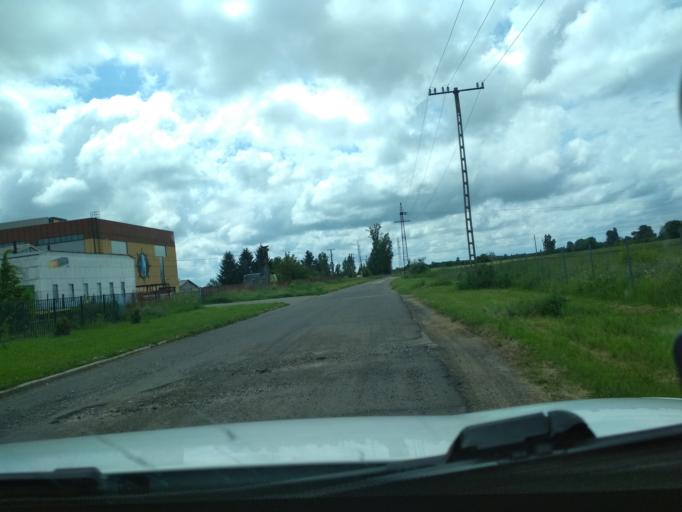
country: HU
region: Jasz-Nagykun-Szolnok
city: Tiszafured
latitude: 47.6078
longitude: 20.7326
